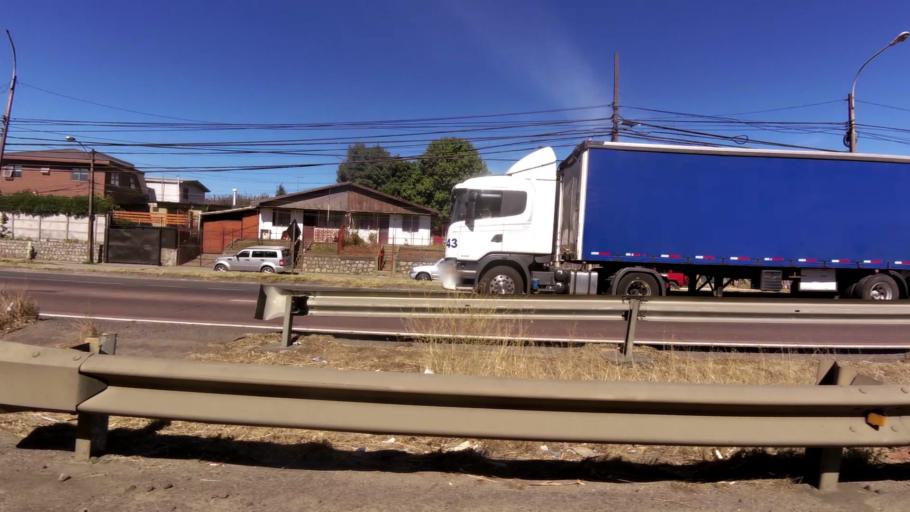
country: CL
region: Biobio
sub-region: Provincia de Concepcion
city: Concepcion
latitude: -36.7884
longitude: -73.0238
